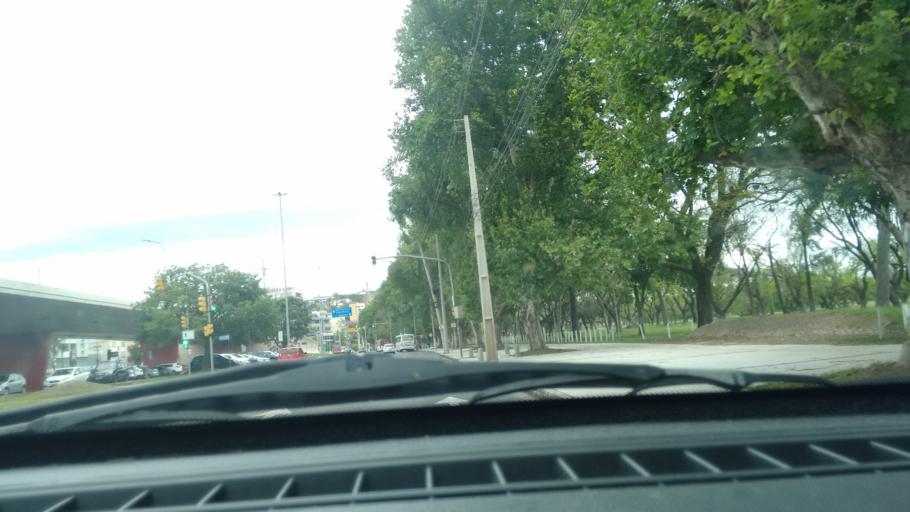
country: BR
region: Rio Grande do Sul
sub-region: Porto Alegre
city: Porto Alegre
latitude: -30.0583
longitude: -51.2308
